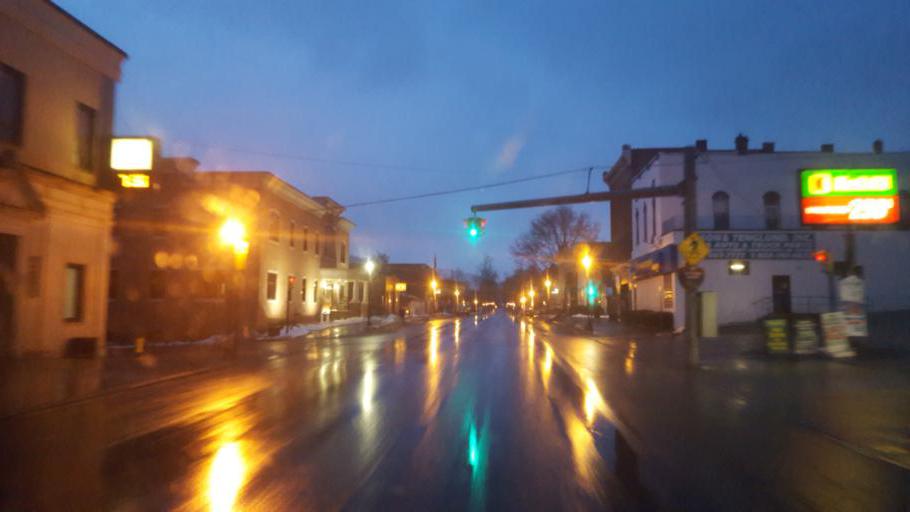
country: US
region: Pennsylvania
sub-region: McKean County
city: Smethport
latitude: 41.8095
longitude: -78.4451
